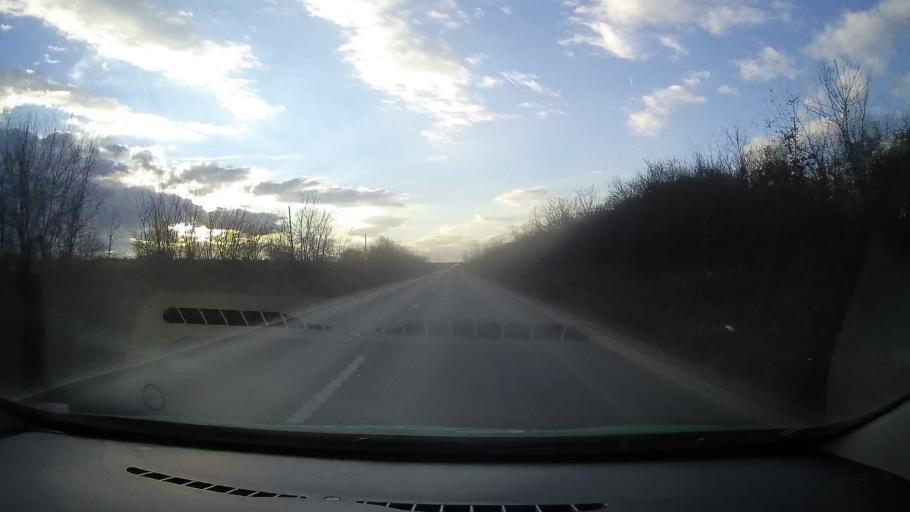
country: RO
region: Dambovita
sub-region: Comuna I. L. Caragiale
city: Mija
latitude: 44.9118
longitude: 25.6814
